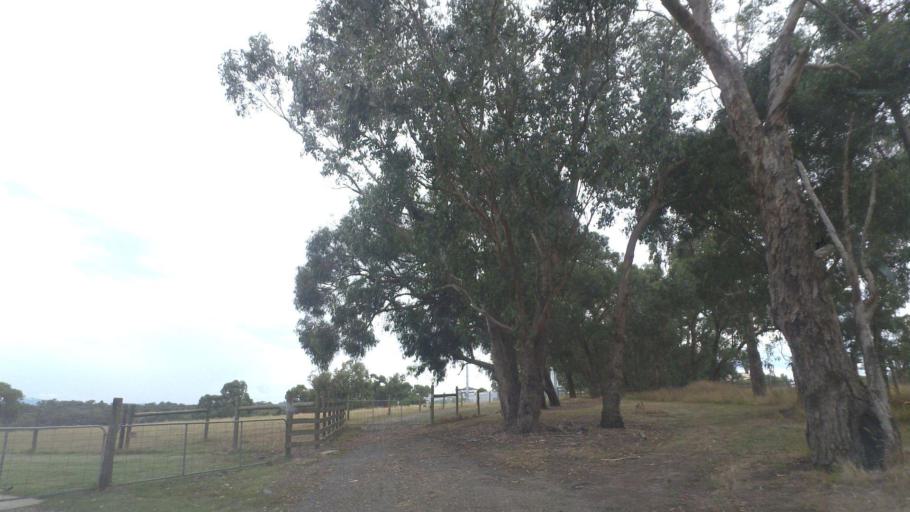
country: AU
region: Victoria
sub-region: Yarra Ranges
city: Mount Evelyn
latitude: -37.7602
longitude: 145.4056
